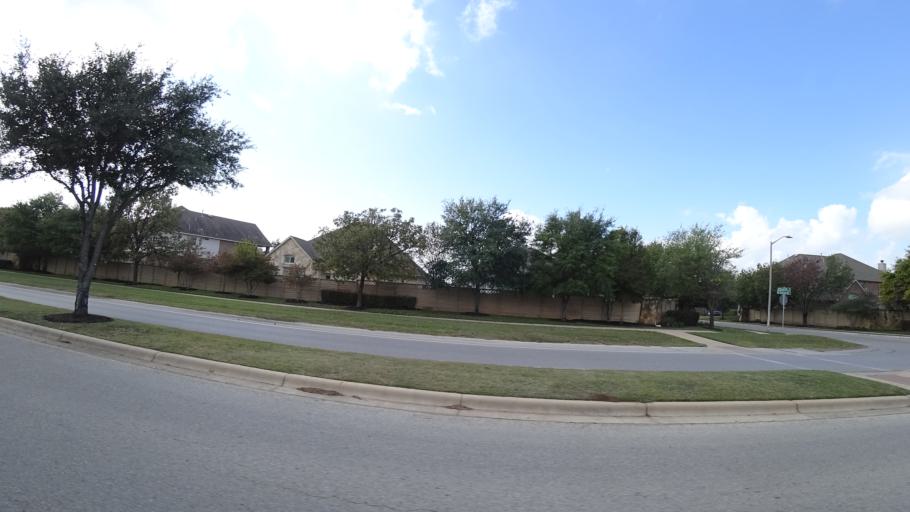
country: US
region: Texas
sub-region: Williamson County
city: Cedar Park
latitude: 30.4782
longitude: -97.8521
